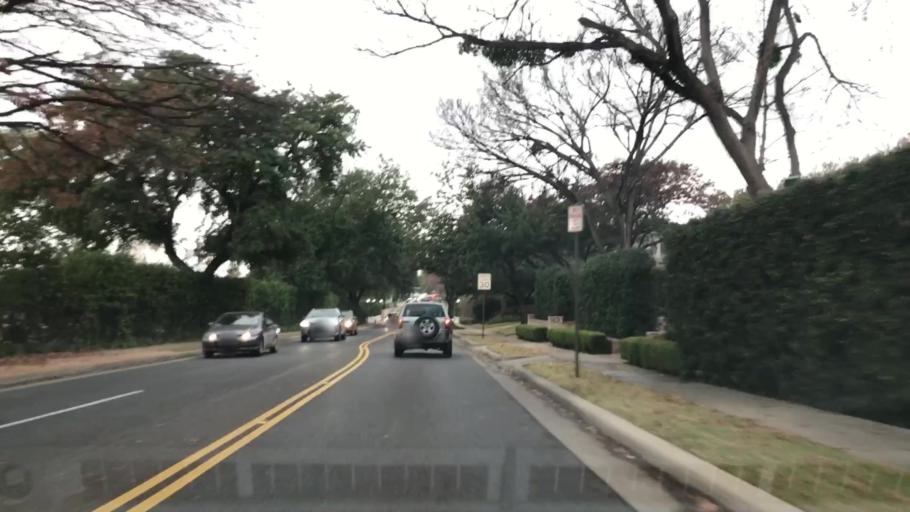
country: US
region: Texas
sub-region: Dallas County
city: Highland Park
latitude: 32.8366
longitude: -96.7991
